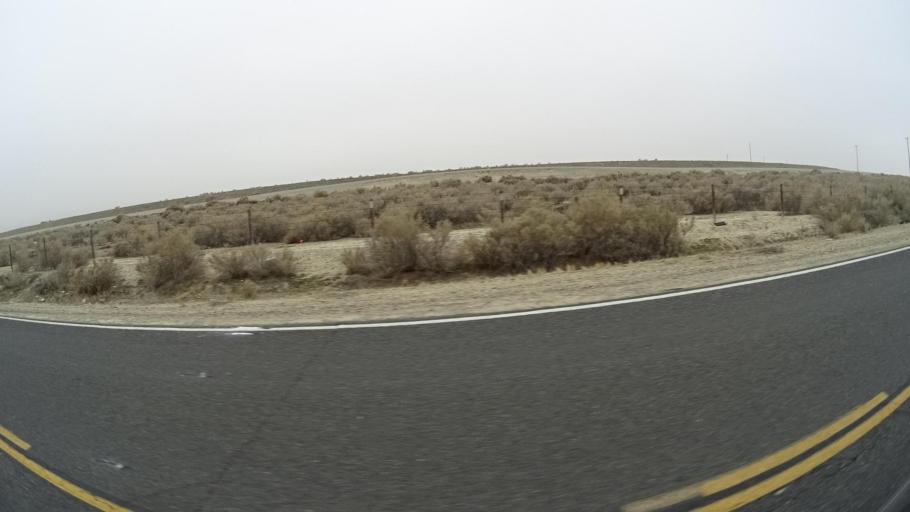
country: US
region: California
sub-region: Kern County
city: Buttonwillow
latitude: 35.3544
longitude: -119.4735
